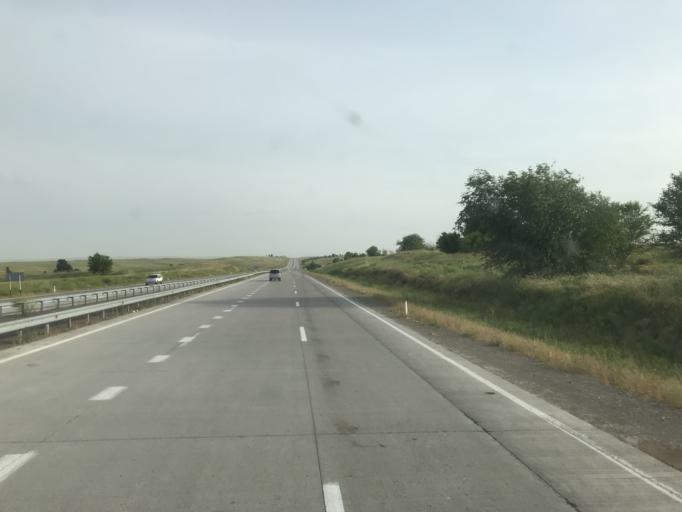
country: KZ
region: Ongtustik Qazaqstan
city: Qazyqurt
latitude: 41.6157
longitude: 69.4030
